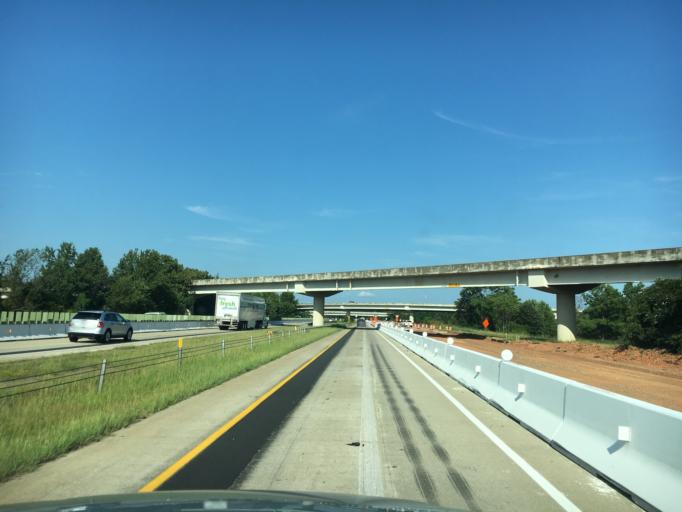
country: US
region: South Carolina
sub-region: Spartanburg County
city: Southern Shops
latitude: 34.9776
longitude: -82.0142
